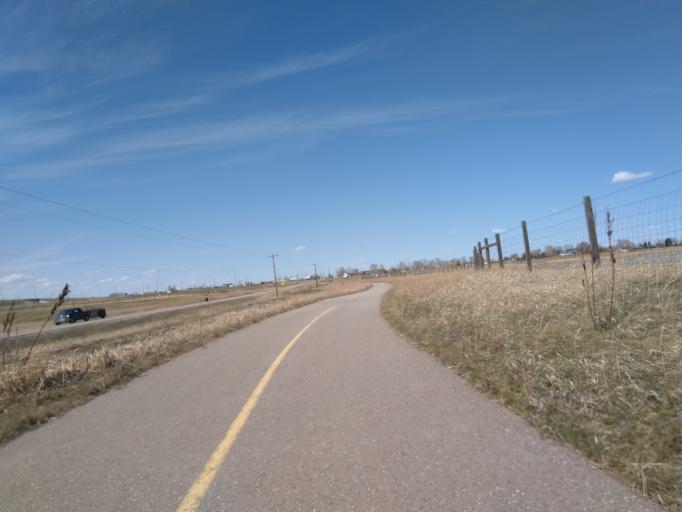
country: CA
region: Alberta
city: Chestermere
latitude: 50.9436
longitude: -113.9114
